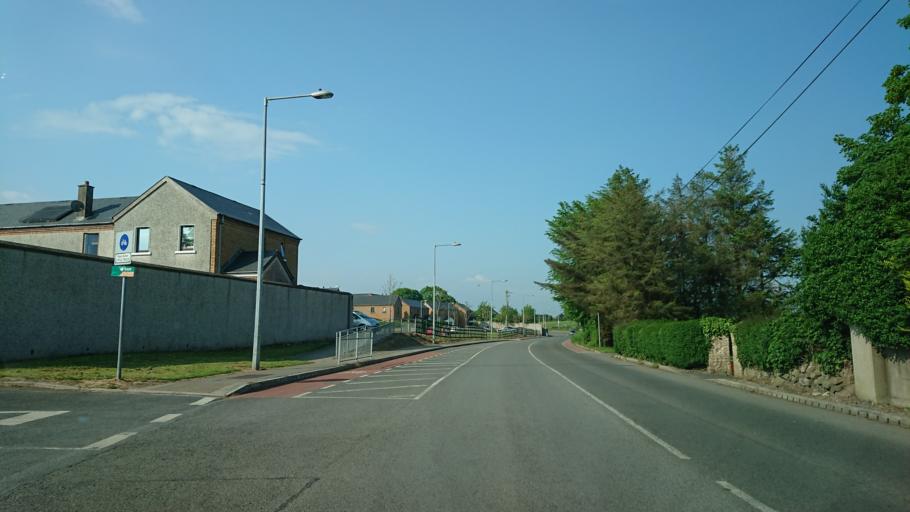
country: IE
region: Munster
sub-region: Waterford
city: Waterford
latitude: 52.2267
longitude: -7.0638
